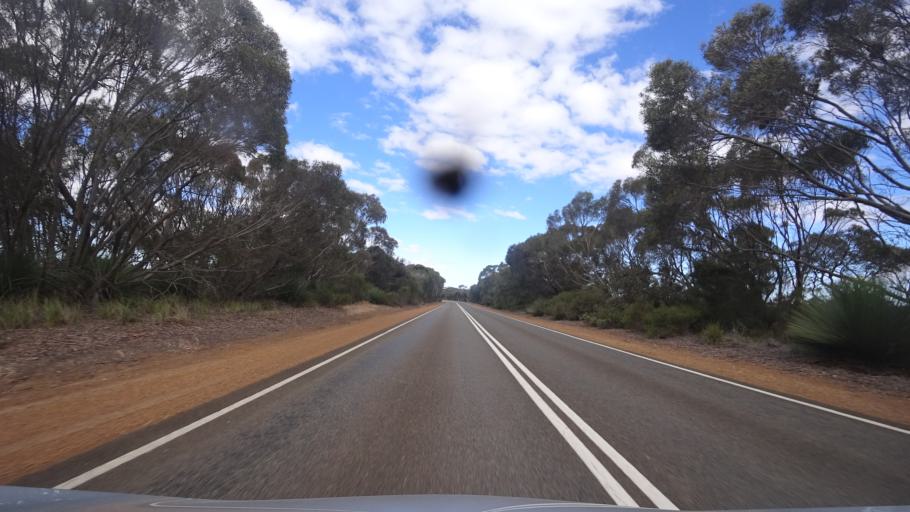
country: AU
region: South Australia
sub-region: Kangaroo Island
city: Kingscote
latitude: -35.7611
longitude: 137.3727
